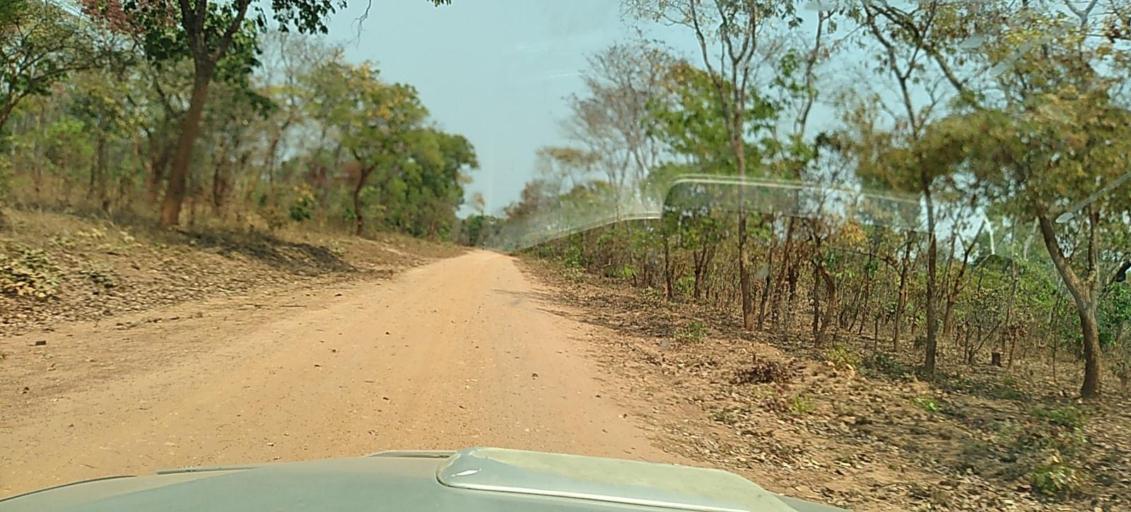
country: ZM
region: North-Western
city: Kasempa
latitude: -13.6896
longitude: 26.3222
